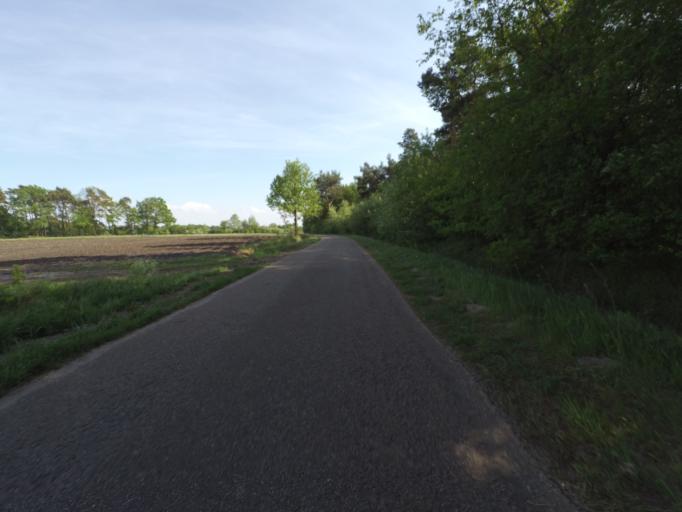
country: NL
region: Overijssel
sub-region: Gemeente Oldenzaal
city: Oldenzaal
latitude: 52.3762
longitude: 6.9557
